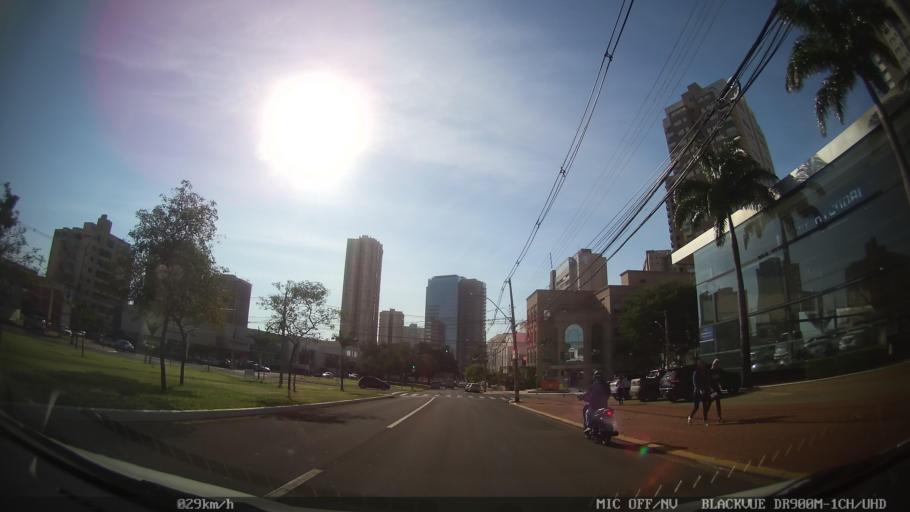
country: BR
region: Sao Paulo
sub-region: Ribeirao Preto
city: Ribeirao Preto
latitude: -21.2109
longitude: -47.8016
